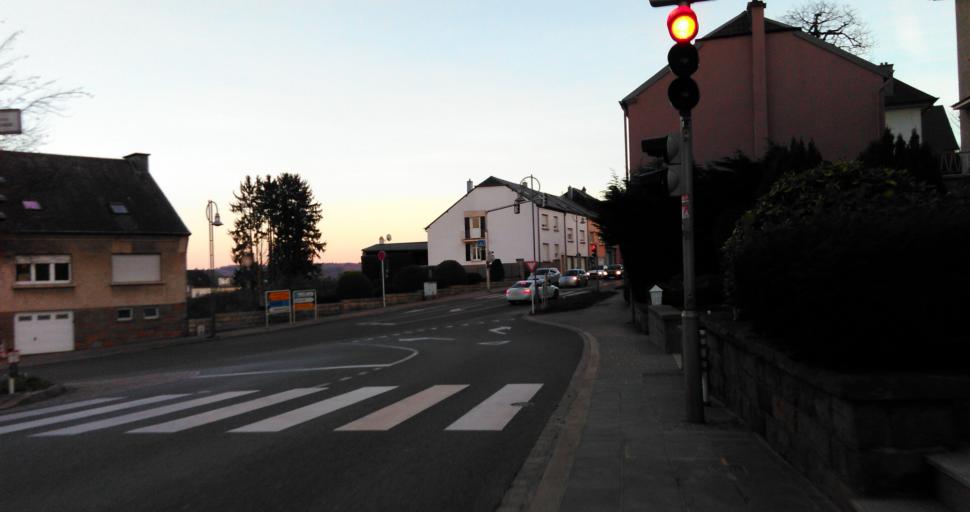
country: LU
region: Luxembourg
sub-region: Canton d'Esch-sur-Alzette
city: Niedercorn
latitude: 49.5397
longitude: 5.8906
